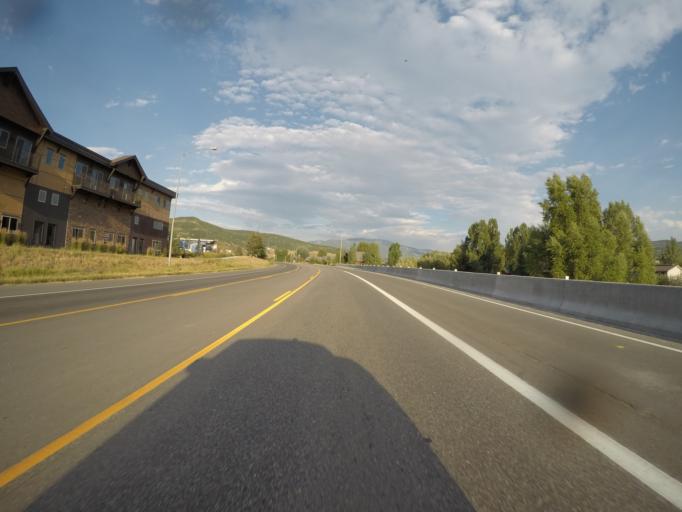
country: US
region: Colorado
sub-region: Routt County
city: Steamboat Springs
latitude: 40.5033
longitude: -106.8660
